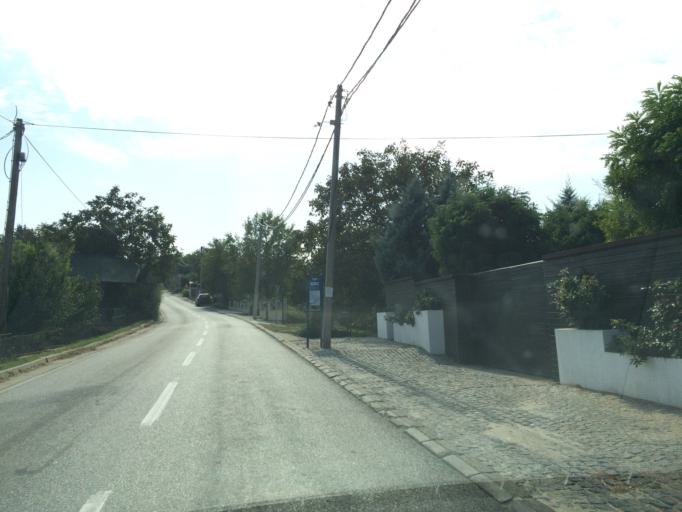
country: RS
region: Autonomna Pokrajina Vojvodina
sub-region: Juznobacki Okrug
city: Novi Sad
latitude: 45.2068
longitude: 19.8331
